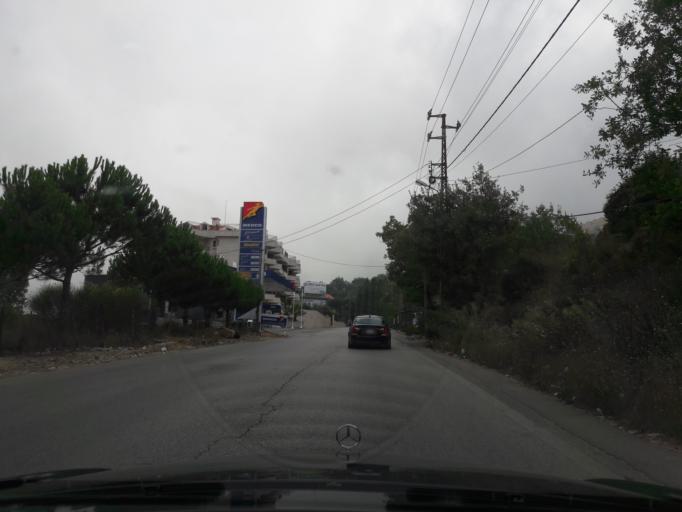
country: LB
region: Mont-Liban
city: Djounie
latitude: 33.9139
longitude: 35.6886
